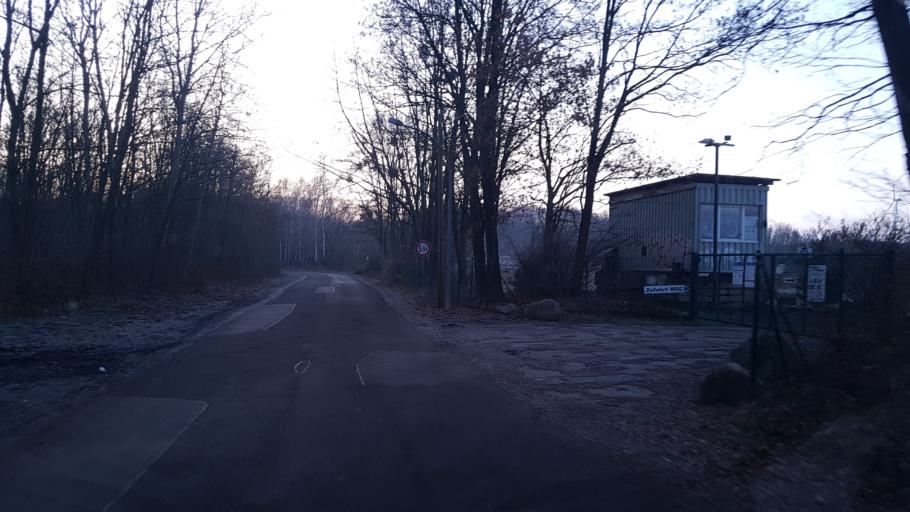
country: DE
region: Brandenburg
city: Schipkau
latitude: 51.5468
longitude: 13.8849
